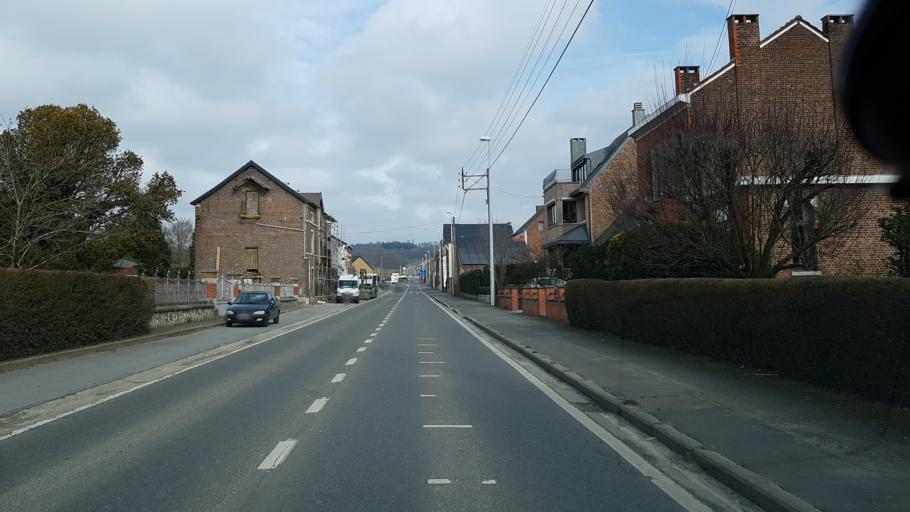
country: BE
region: Wallonia
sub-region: Province de Liege
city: Wanze
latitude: 50.5439
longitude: 5.2217
